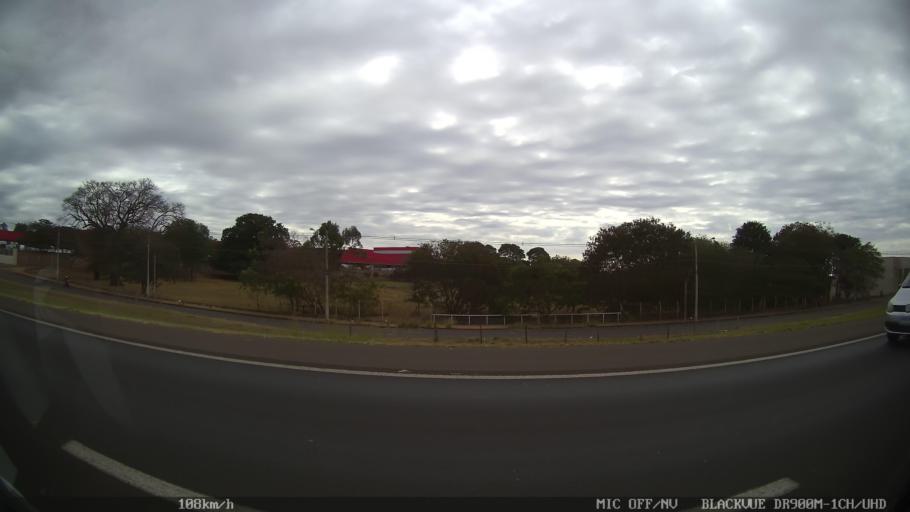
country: BR
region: Sao Paulo
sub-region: Bady Bassitt
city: Bady Bassitt
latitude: -20.8068
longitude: -49.5130
